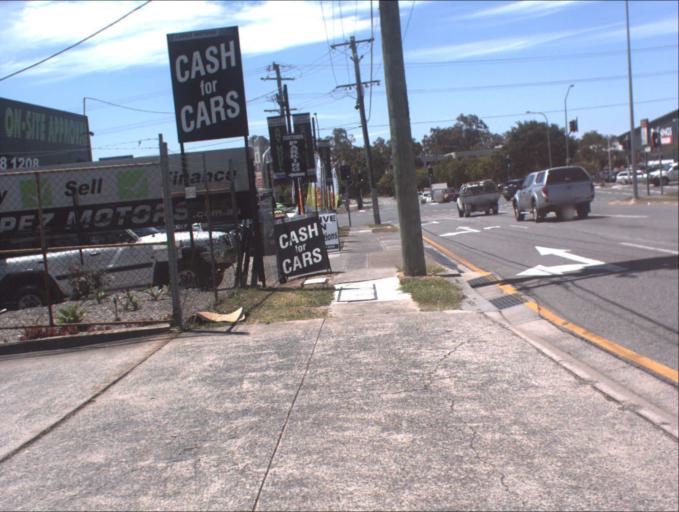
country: AU
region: Queensland
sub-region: Logan
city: Woodridge
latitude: -27.6202
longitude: 153.1110
